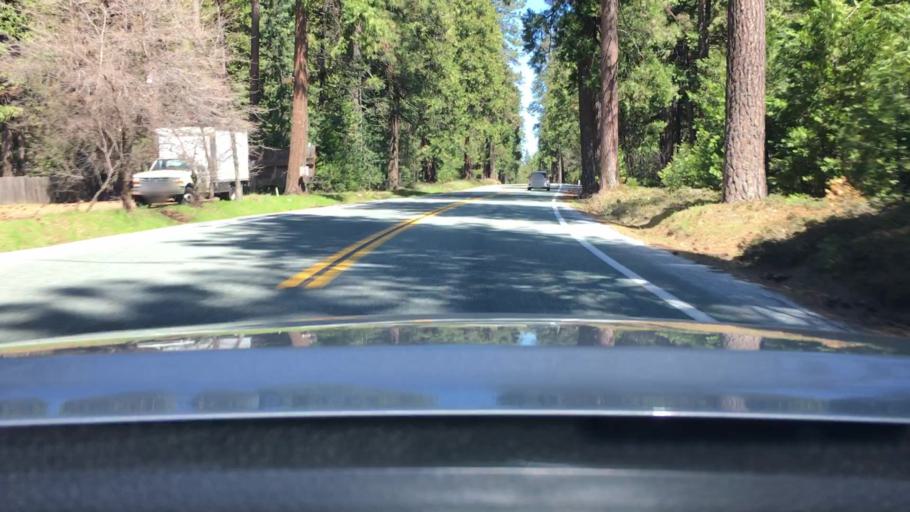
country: US
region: California
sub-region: Amador County
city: Pioneer
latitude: 38.4754
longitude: -120.5256
